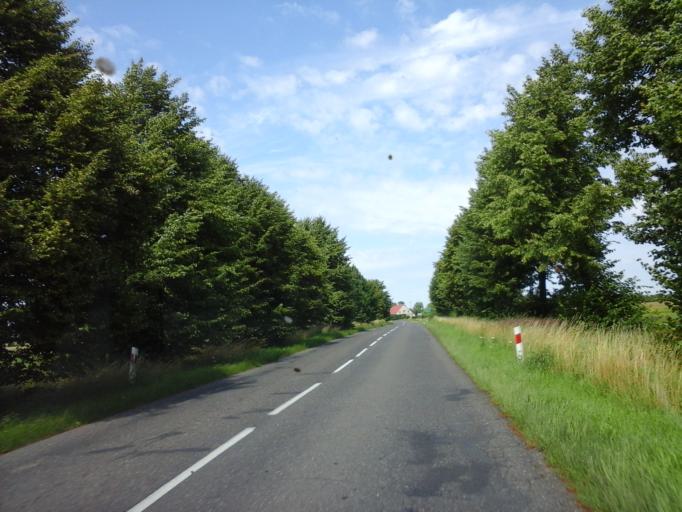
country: PL
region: West Pomeranian Voivodeship
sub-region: Powiat choszczenski
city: Bierzwnik
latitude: 53.0176
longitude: 15.7152
